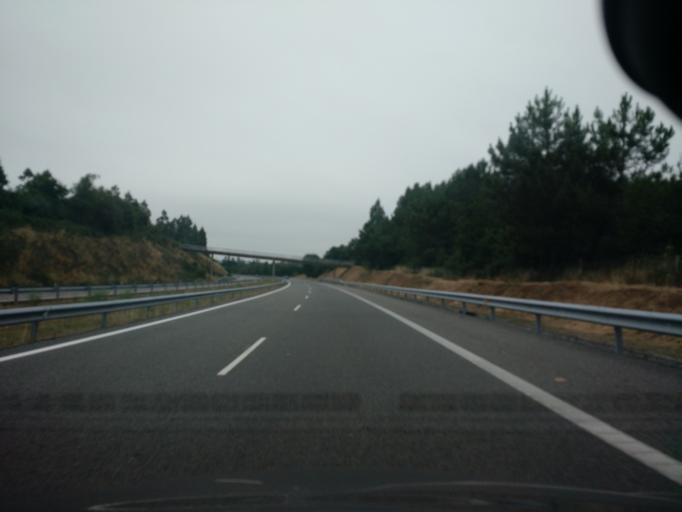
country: ES
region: Galicia
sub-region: Provincia da Coruna
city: Ordes
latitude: 43.0355
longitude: -8.3940
